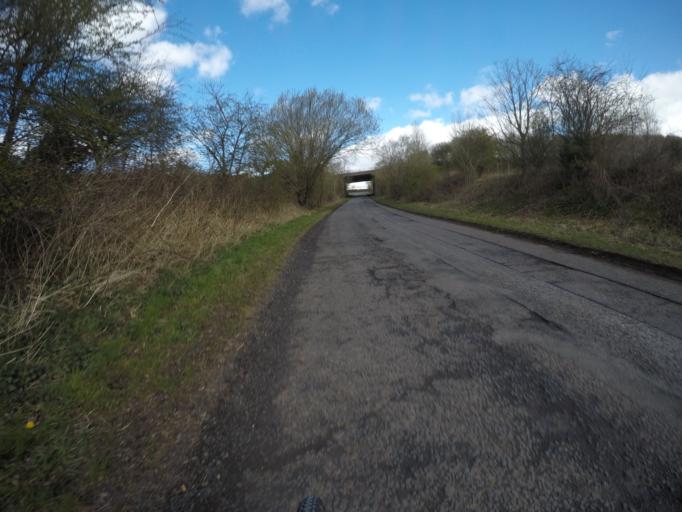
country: GB
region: Scotland
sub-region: East Ayrshire
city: Crosshouse
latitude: 55.6039
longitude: -4.5743
